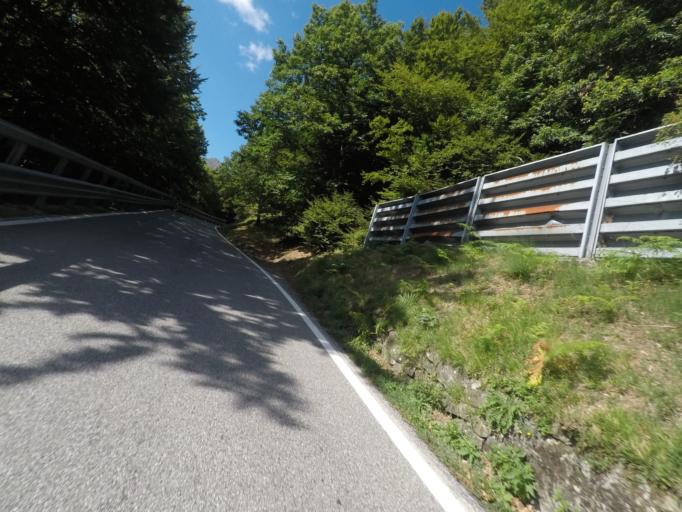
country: IT
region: Tuscany
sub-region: Provincia di Massa-Carrara
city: Comano
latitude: 44.2884
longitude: 10.2055
